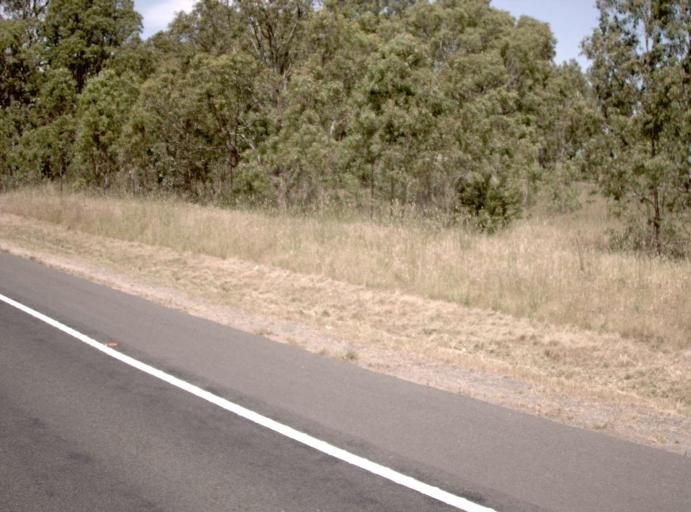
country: AU
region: Victoria
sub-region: Latrobe
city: Traralgon
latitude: -38.1790
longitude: 146.6285
